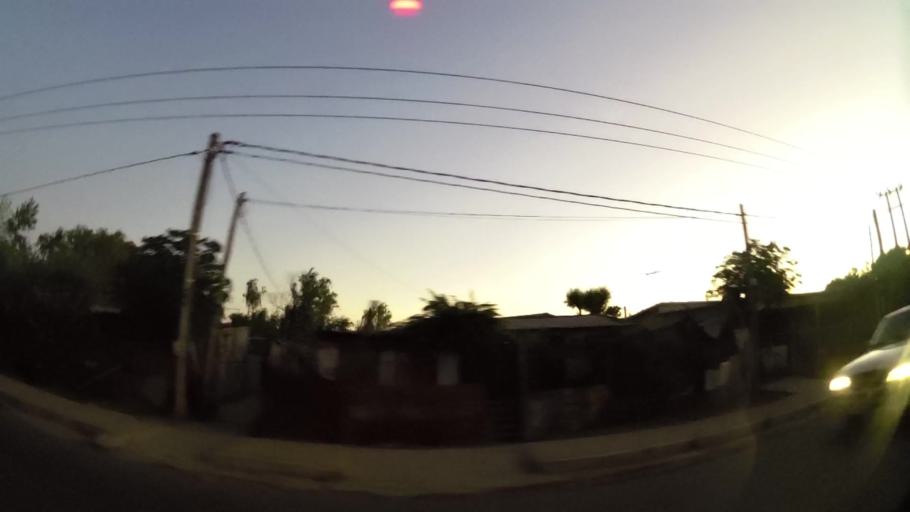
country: UY
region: Canelones
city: La Paz
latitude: -34.8254
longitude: -56.1812
